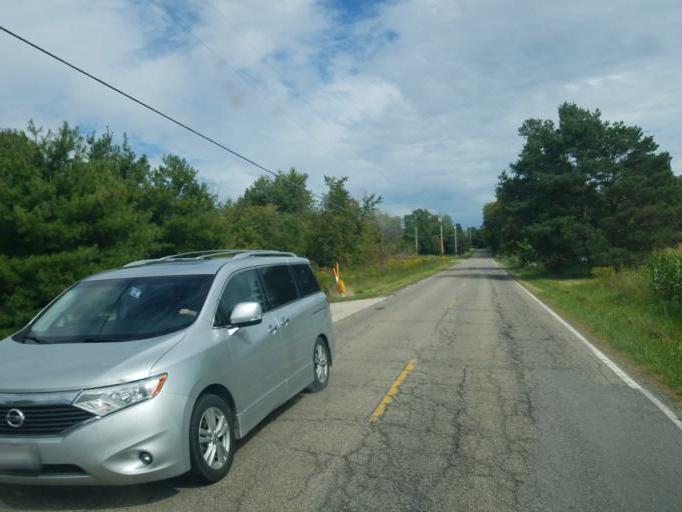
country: US
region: Ohio
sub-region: Licking County
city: Johnstown
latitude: 40.0956
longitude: -82.7166
